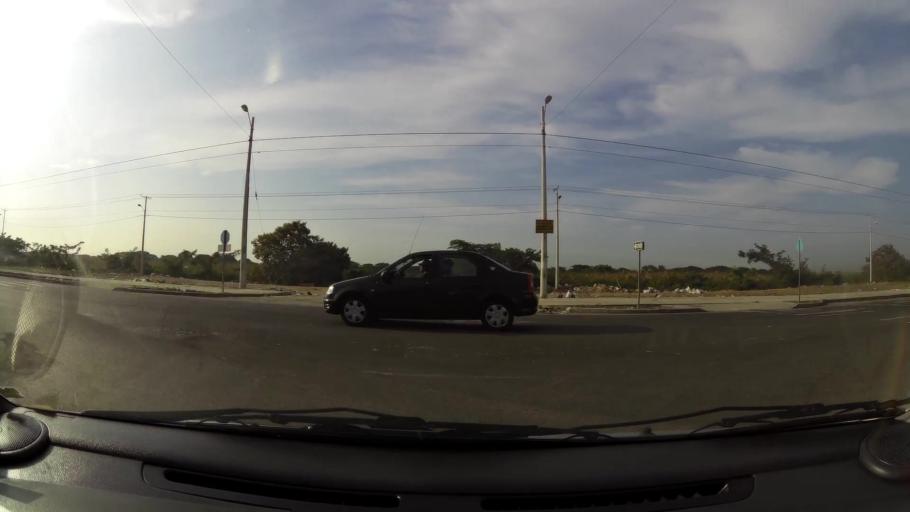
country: EC
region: Guayas
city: Eloy Alfaro
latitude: -2.0660
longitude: -79.8918
